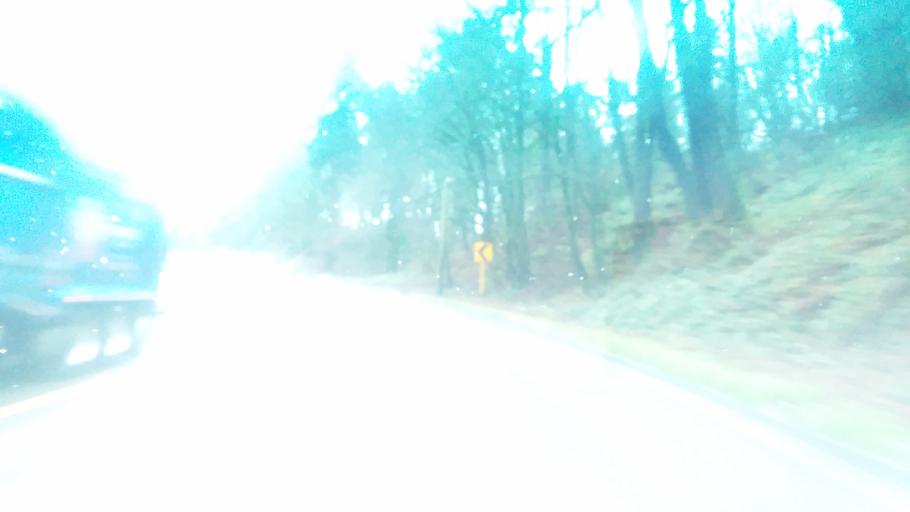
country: US
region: Washington
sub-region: King County
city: Kent
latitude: 47.4127
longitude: -122.2144
